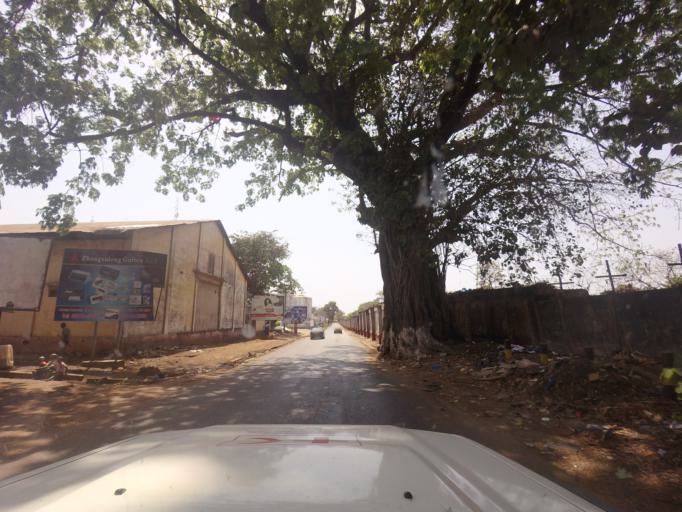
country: GN
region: Conakry
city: Camayenne
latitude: 9.5157
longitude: -13.7092
